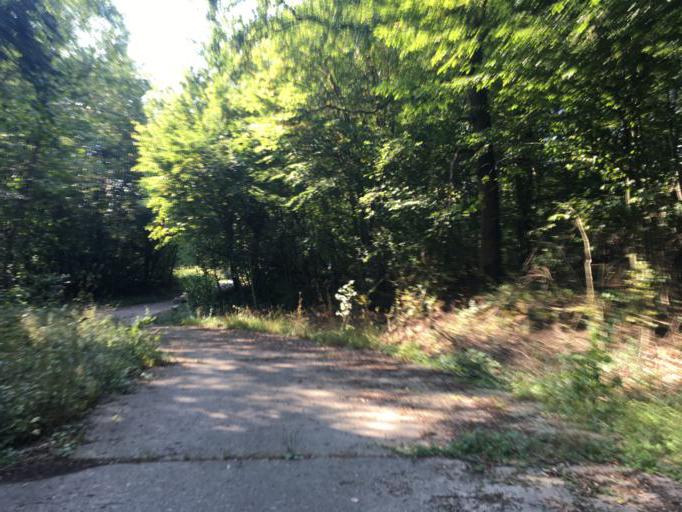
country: DE
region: Baden-Wuerttemberg
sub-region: Tuebingen Region
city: Kusterdingen
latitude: 48.5064
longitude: 9.0898
